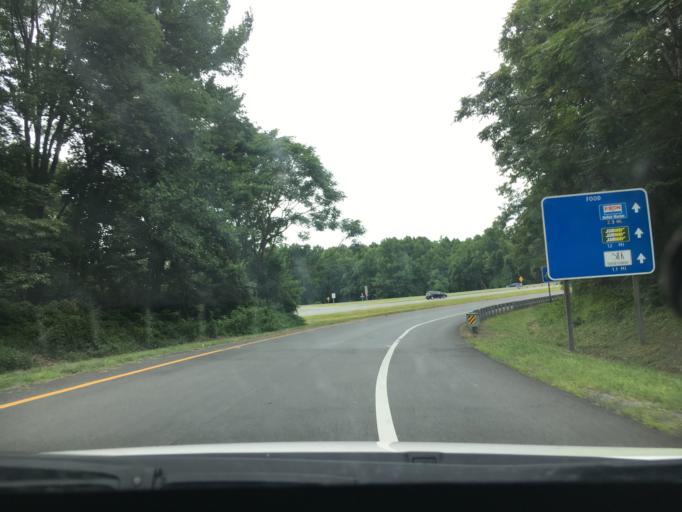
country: US
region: Virginia
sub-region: City of Charlottesville
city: Charlottesville
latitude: 38.0205
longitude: -78.5351
